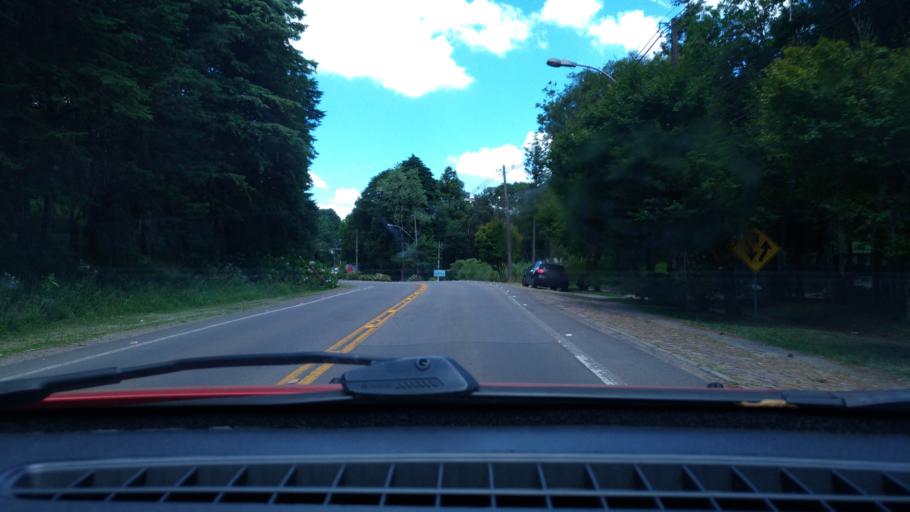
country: BR
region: Rio Grande do Sul
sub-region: Canela
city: Canela
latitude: -29.3556
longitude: -50.8299
